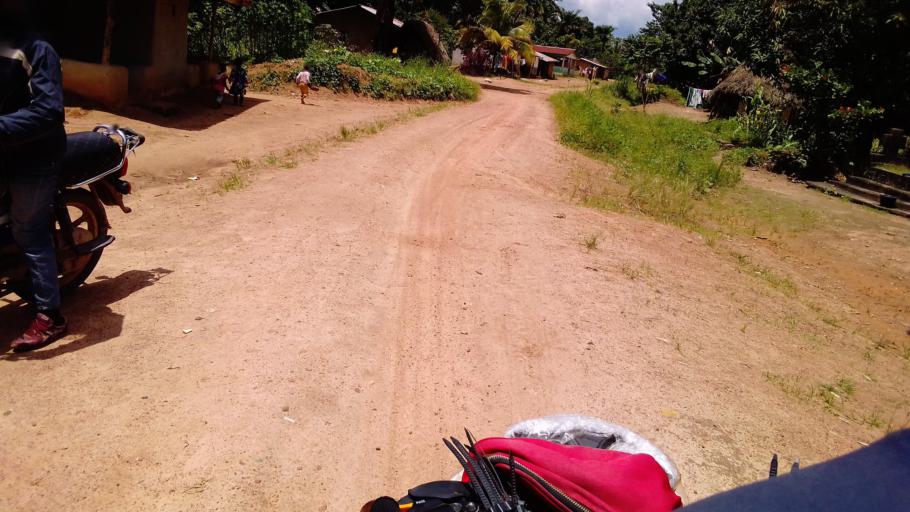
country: SL
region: Eastern Province
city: Koidu
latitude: 8.6980
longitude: -10.9536
